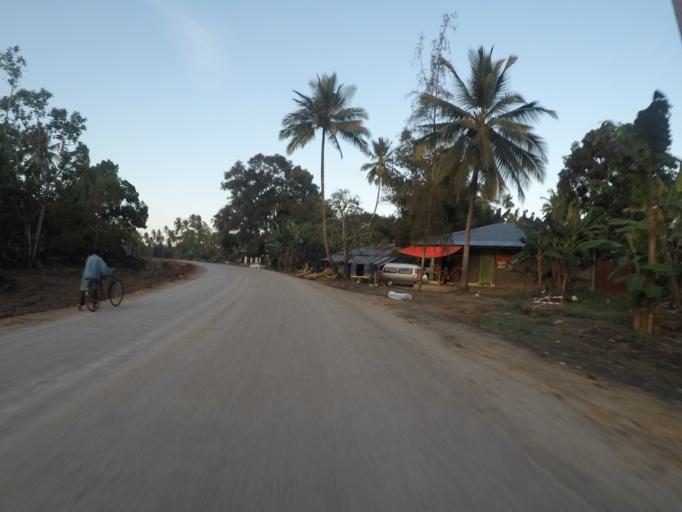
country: TZ
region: Zanzibar North
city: Gamba
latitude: -5.9832
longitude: 39.2859
